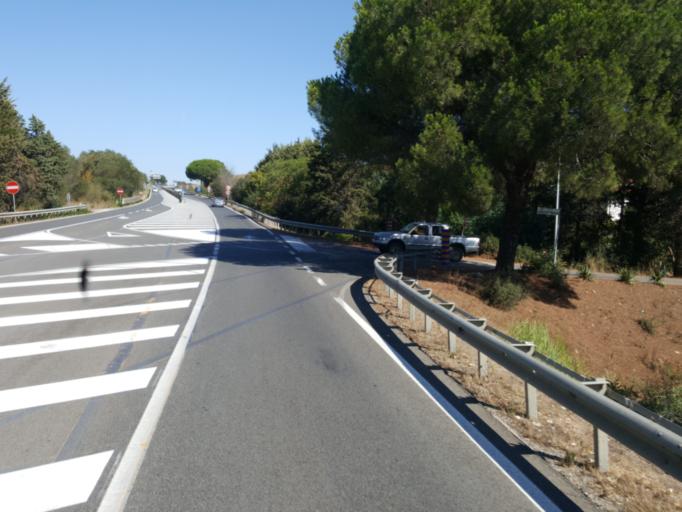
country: IT
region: Tuscany
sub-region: Provincia di Grosseto
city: Fonteblanda
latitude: 42.5511
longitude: 11.1738
